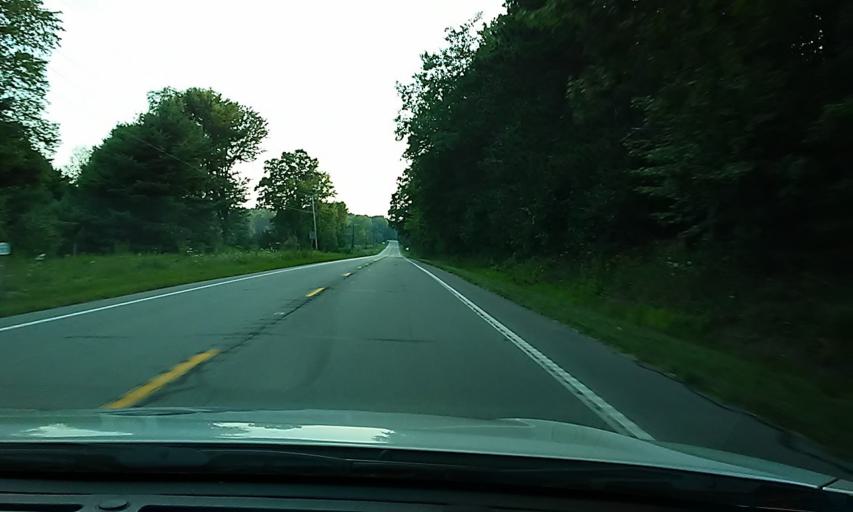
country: US
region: Pennsylvania
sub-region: Forest County
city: Marienville
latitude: 41.4258
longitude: -79.1996
